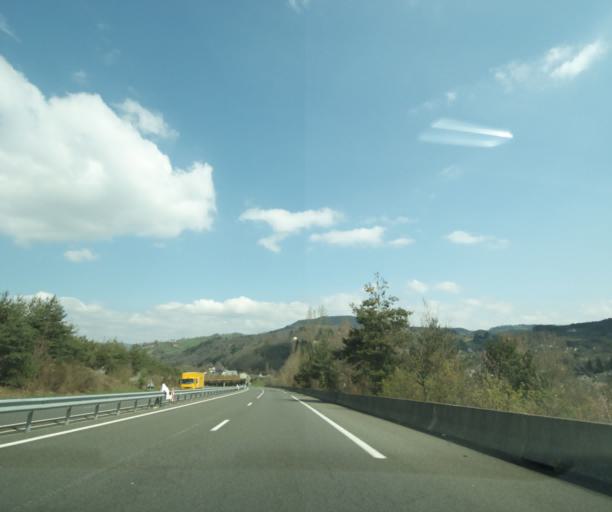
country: FR
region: Languedoc-Roussillon
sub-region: Departement de la Lozere
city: La Canourgue
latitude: 44.4330
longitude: 3.1941
